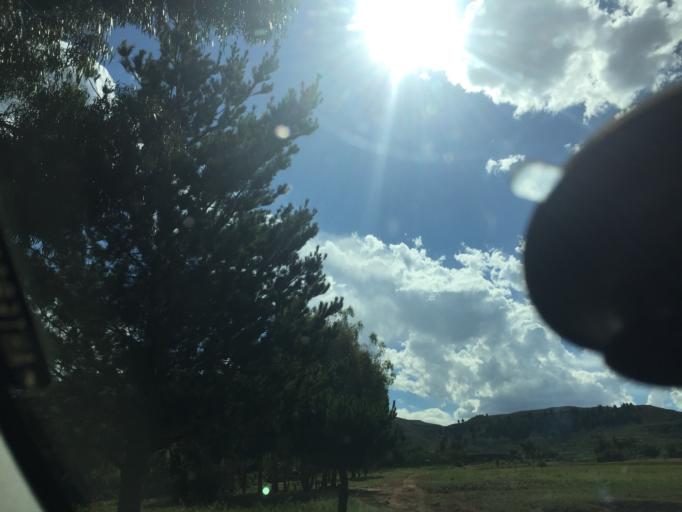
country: LS
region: Maseru
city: Nako
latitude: -29.5902
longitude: 27.7585
